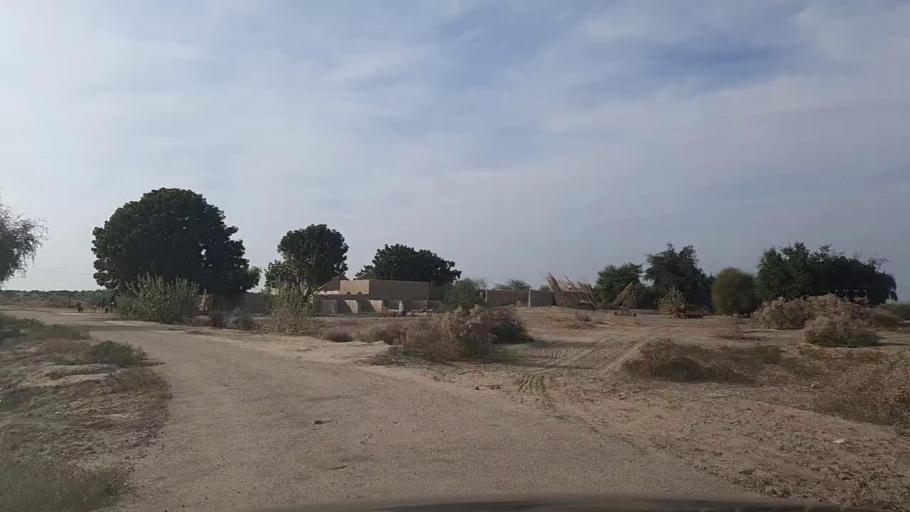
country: PK
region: Sindh
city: Jam Sahib
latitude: 26.4471
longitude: 68.6124
